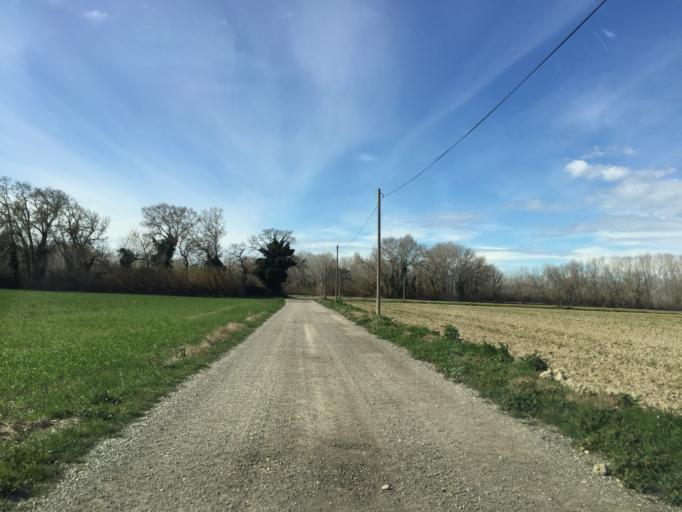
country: FR
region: Provence-Alpes-Cote d'Azur
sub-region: Departement du Vaucluse
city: Caderousse
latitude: 44.1424
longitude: 4.7351
